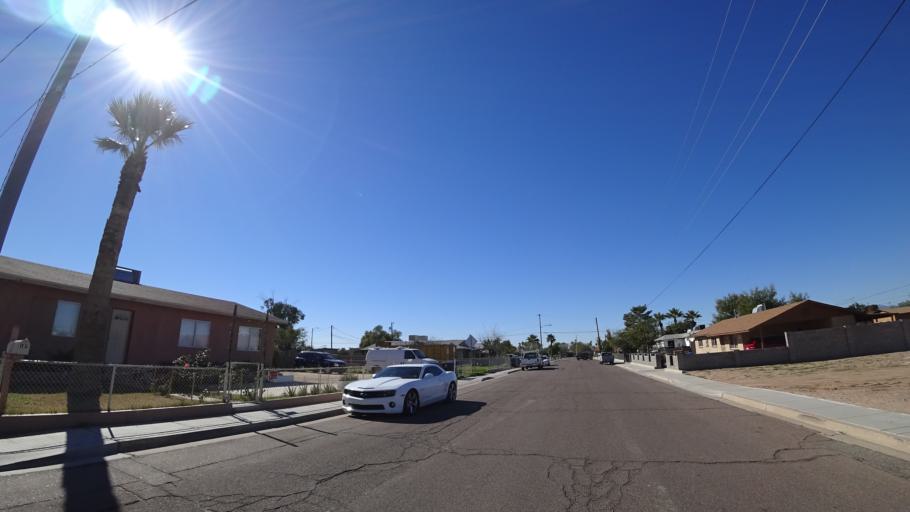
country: US
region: Arizona
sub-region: Maricopa County
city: Avondale
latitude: 33.4245
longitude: -112.3473
